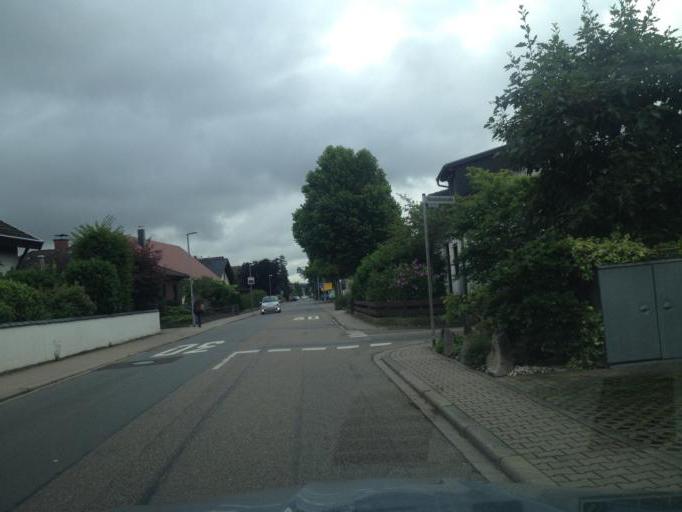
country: DE
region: Baden-Wuerttemberg
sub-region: Karlsruhe Region
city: Walldorf
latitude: 49.3086
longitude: 8.6334
